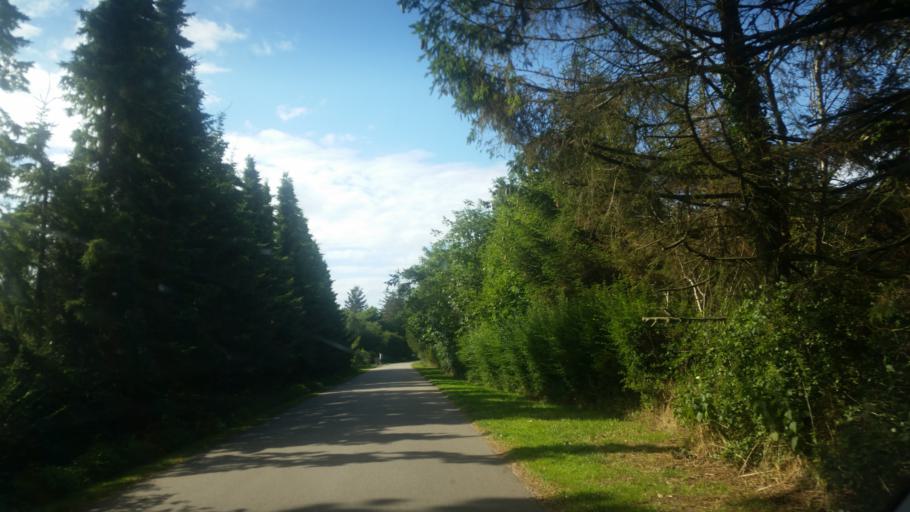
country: DK
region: Zealand
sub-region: Odsherred Kommune
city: Horve
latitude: 55.8268
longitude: 11.3979
